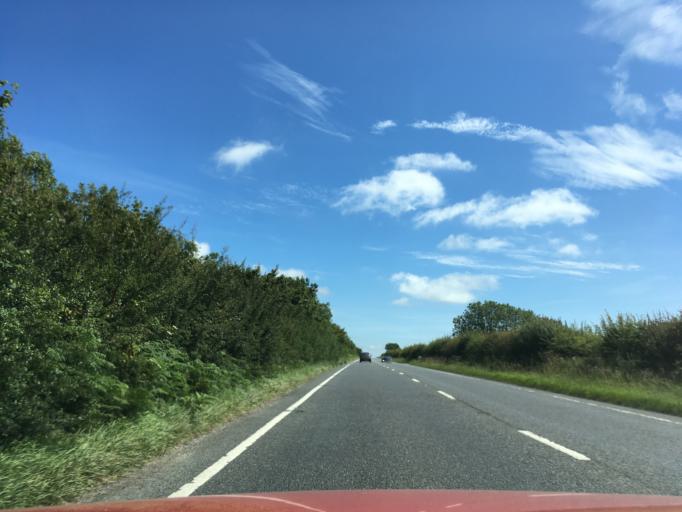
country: GB
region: England
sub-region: Dorset
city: Sherborne
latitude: 50.8081
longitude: -2.5529
